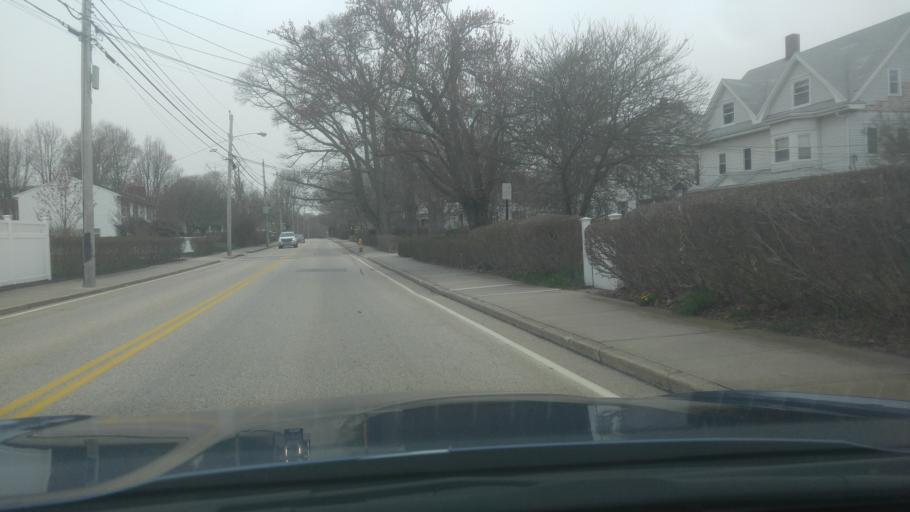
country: US
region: Rhode Island
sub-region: Washington County
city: Narragansett Pier
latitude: 41.4314
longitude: -71.4614
